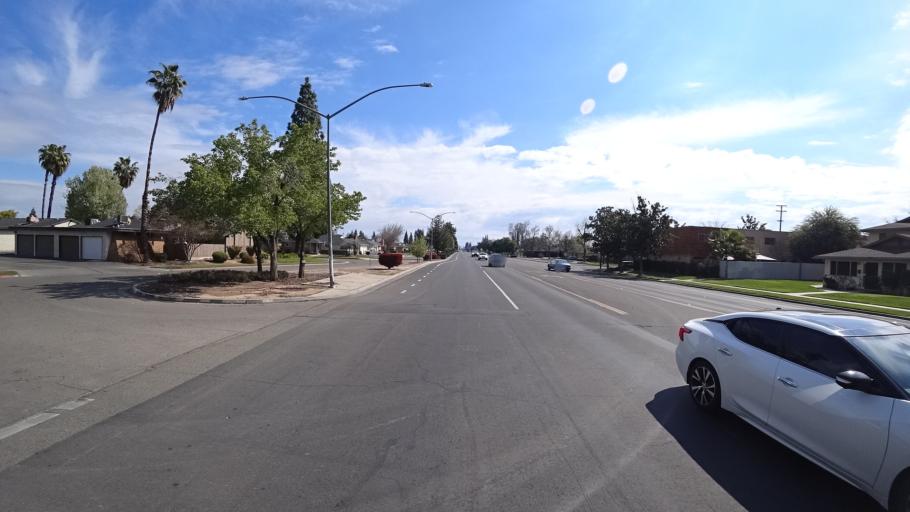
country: US
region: California
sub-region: Fresno County
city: Fresno
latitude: 36.8158
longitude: -119.7776
